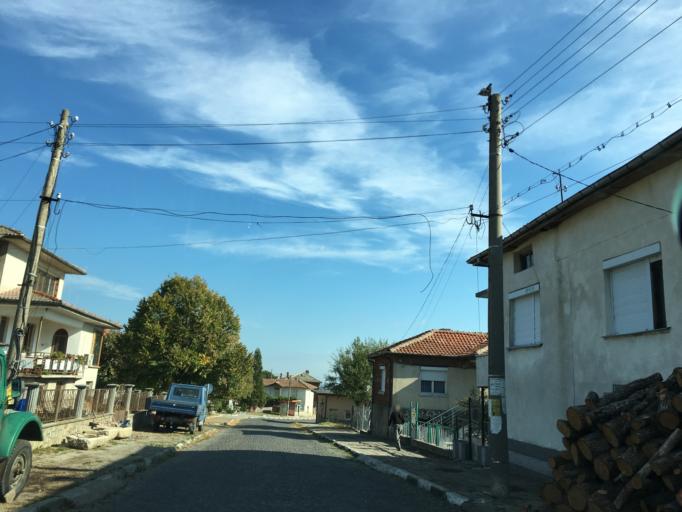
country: BG
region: Khaskovo
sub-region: Obshtina Ivaylovgrad
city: Ivaylovgrad
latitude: 41.5131
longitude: 26.1126
